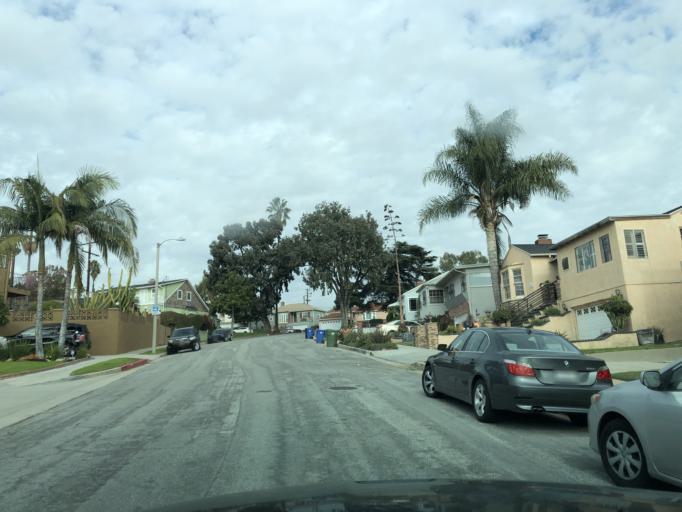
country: US
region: California
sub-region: Los Angeles County
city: View Park-Windsor Hills
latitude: 33.9936
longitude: -118.3569
